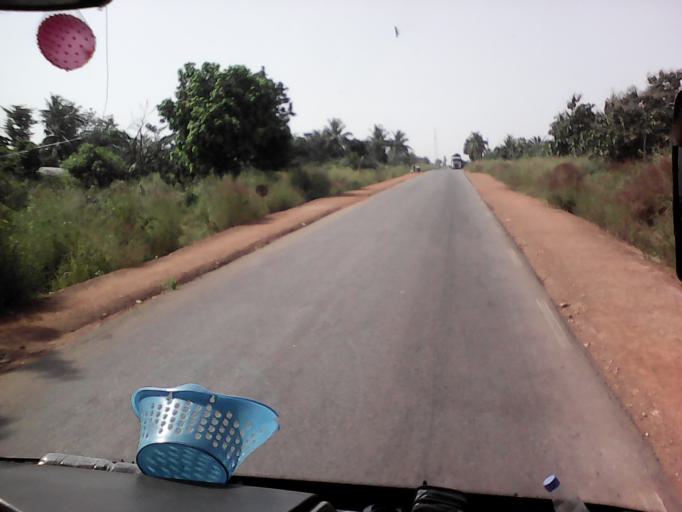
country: TG
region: Centrale
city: Sotouboua
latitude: 8.7379
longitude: 1.0516
